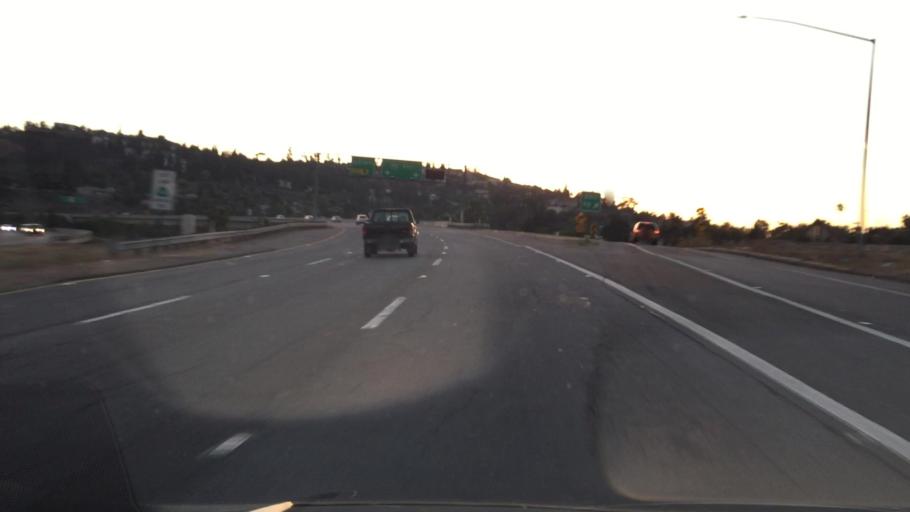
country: US
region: California
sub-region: San Diego County
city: Spring Valley
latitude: 32.7537
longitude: -117.0076
